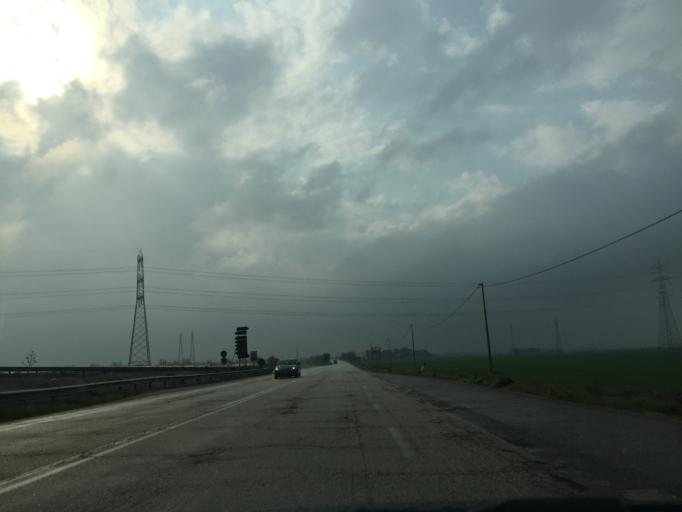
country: IT
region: Apulia
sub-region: Provincia di Foggia
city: Foggia
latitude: 41.4976
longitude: 15.5193
